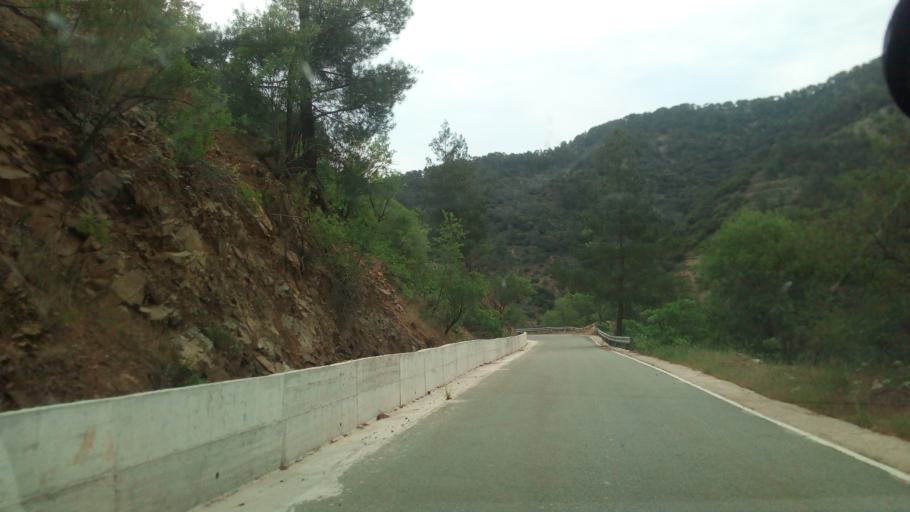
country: CY
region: Lefkosia
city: Kakopetria
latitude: 34.9682
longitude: 32.7515
